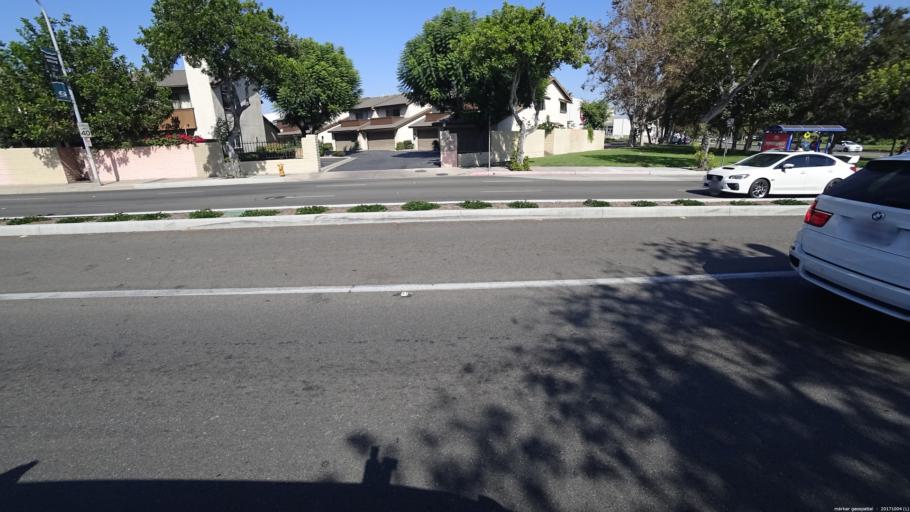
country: US
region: California
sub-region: Orange County
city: Garden Grove
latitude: 33.7777
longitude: -117.9388
